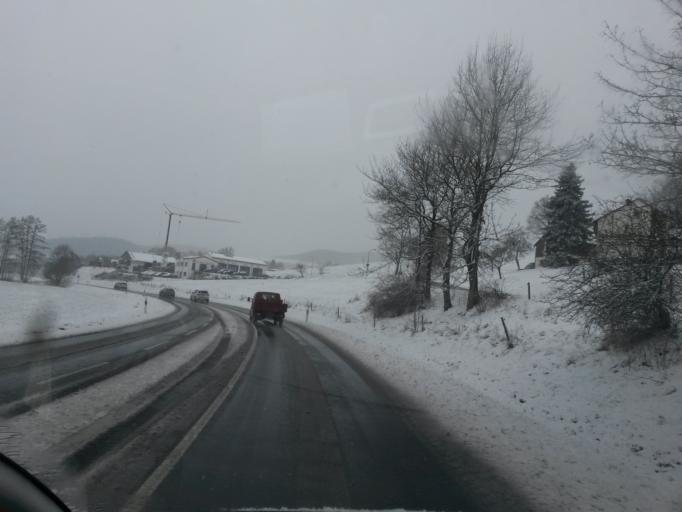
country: DE
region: Hesse
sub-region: Regierungsbezirk Kassel
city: Poppenhausen
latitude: 50.4917
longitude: 9.8551
